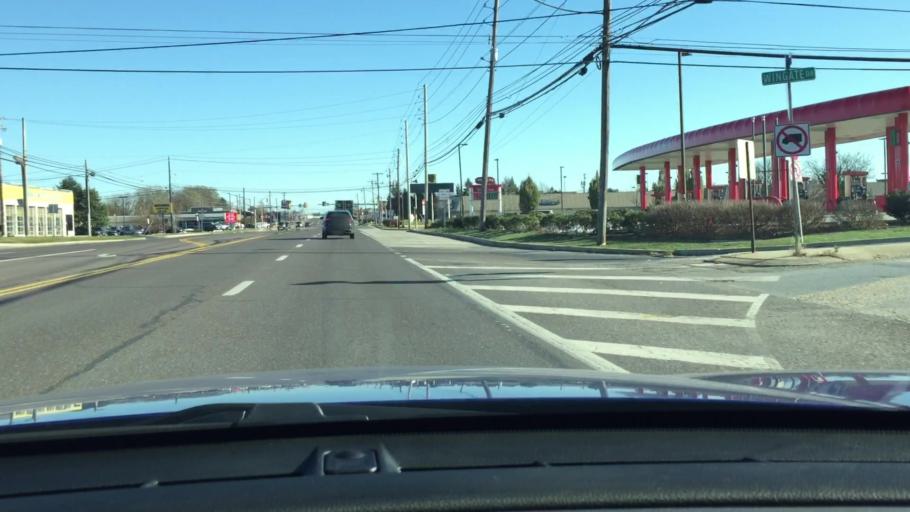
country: US
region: Pennsylvania
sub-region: Cumberland County
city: Mechanicsburg
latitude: 40.2435
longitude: -76.9931
